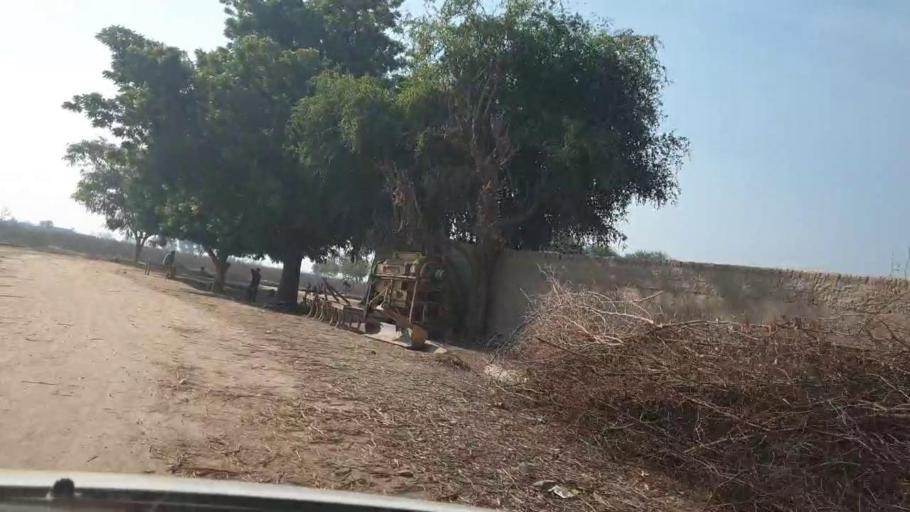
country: PK
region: Sindh
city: Bhan
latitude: 26.6201
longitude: 67.7588
